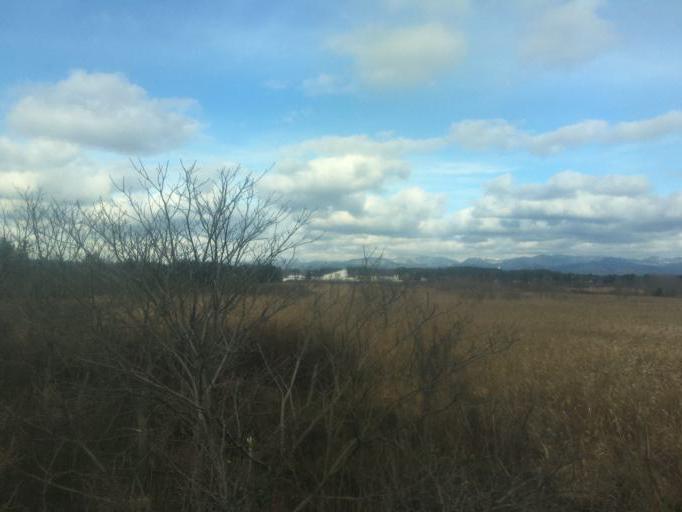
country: JP
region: Akita
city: Noshiromachi
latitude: 40.1950
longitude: 140.0820
